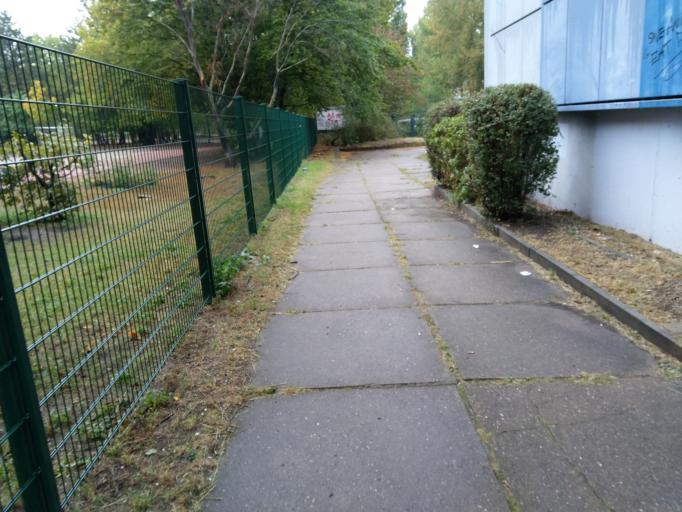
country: DE
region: Berlin
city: Karlshorst
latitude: 52.4900
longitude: 13.5210
